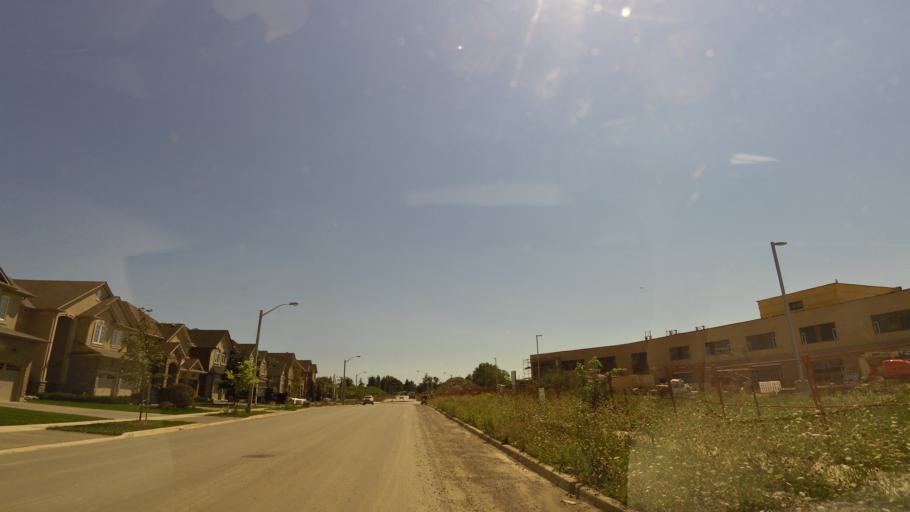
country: CA
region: Ontario
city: Ancaster
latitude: 43.2132
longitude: -79.9356
